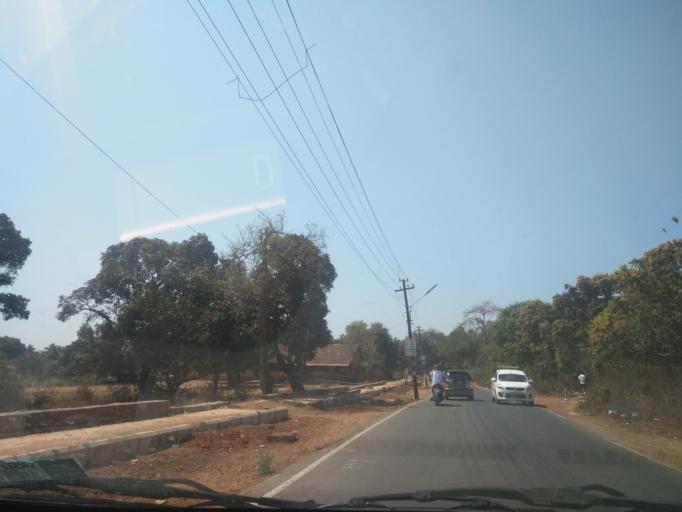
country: IN
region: Goa
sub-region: North Goa
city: Morjim
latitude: 15.6401
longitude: 73.7574
